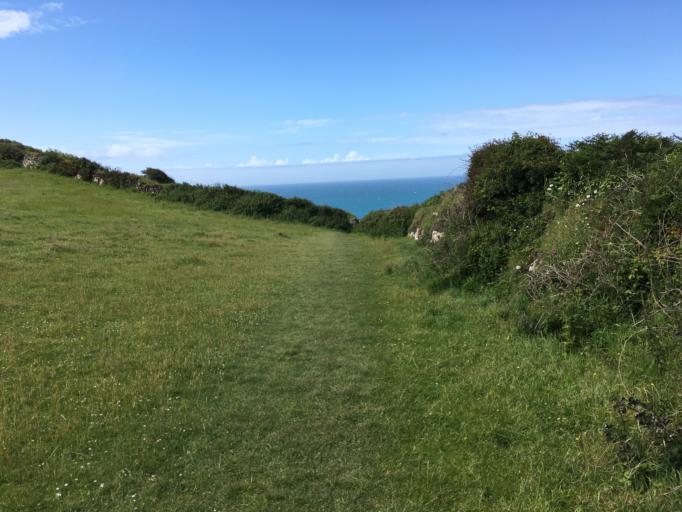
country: GB
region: England
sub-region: Cornwall
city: Camelford
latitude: 50.6944
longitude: -4.6845
